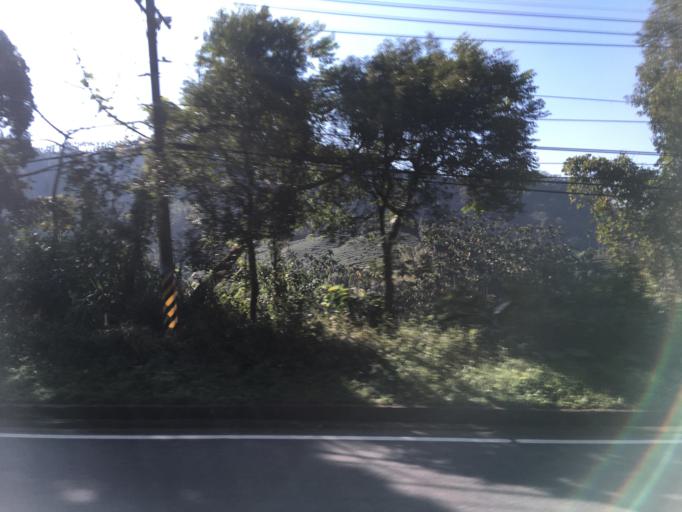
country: TW
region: Taiwan
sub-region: Chiayi
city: Jiayi Shi
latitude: 23.4225
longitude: 120.6433
